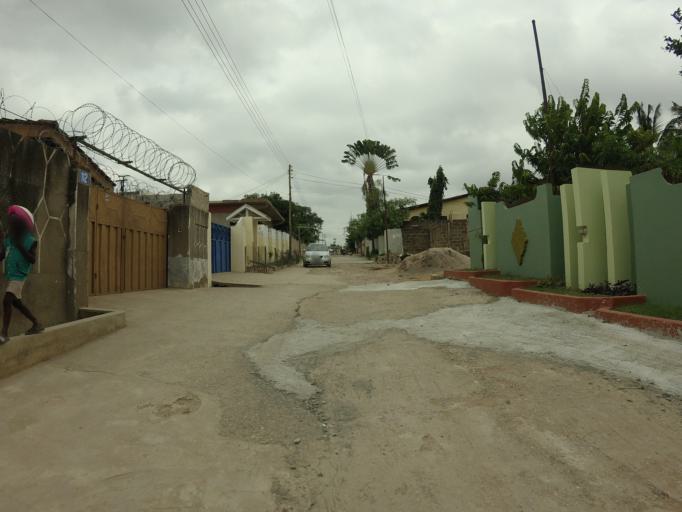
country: GH
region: Greater Accra
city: Dome
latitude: 5.6357
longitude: -0.2322
